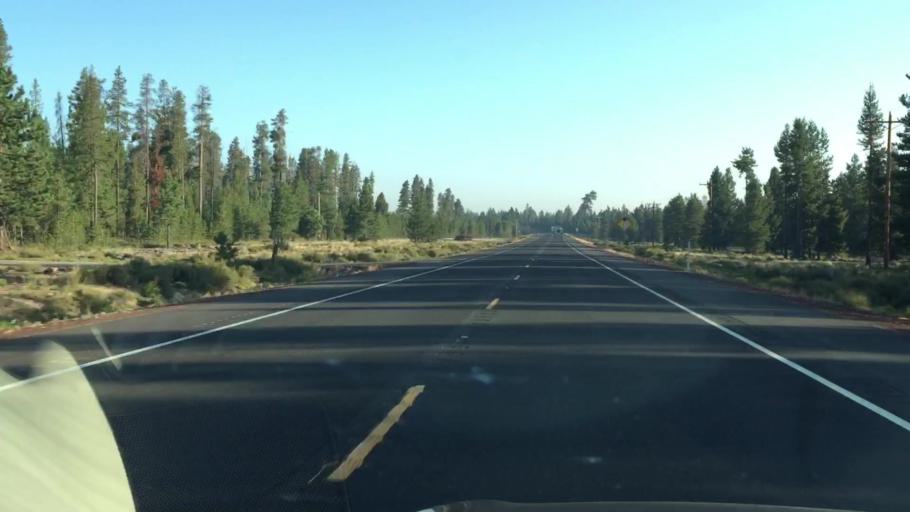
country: US
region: Oregon
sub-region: Deschutes County
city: La Pine
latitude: 43.2011
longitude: -121.7797
